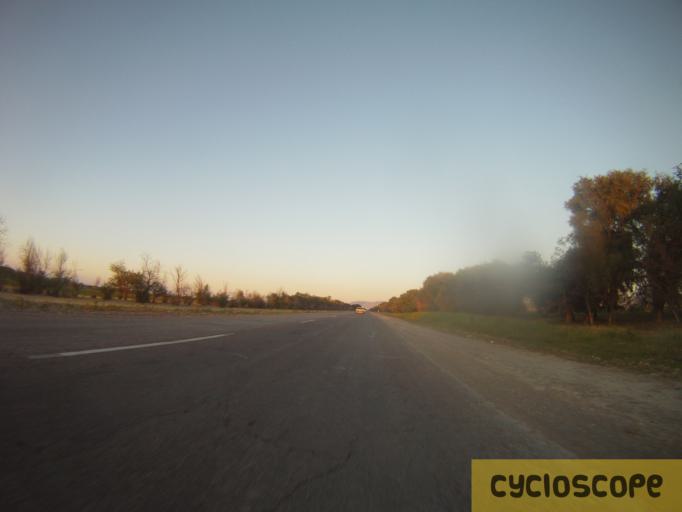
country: KZ
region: Almaty Oblysy
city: Turgen'
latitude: 43.5604
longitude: 78.3671
